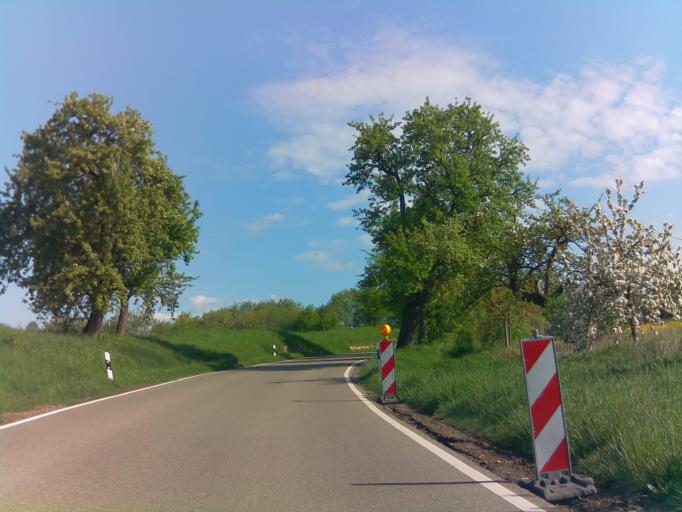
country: DE
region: Baden-Wuerttemberg
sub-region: Regierungsbezirk Stuttgart
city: Motzingen
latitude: 48.5000
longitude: 8.7740
